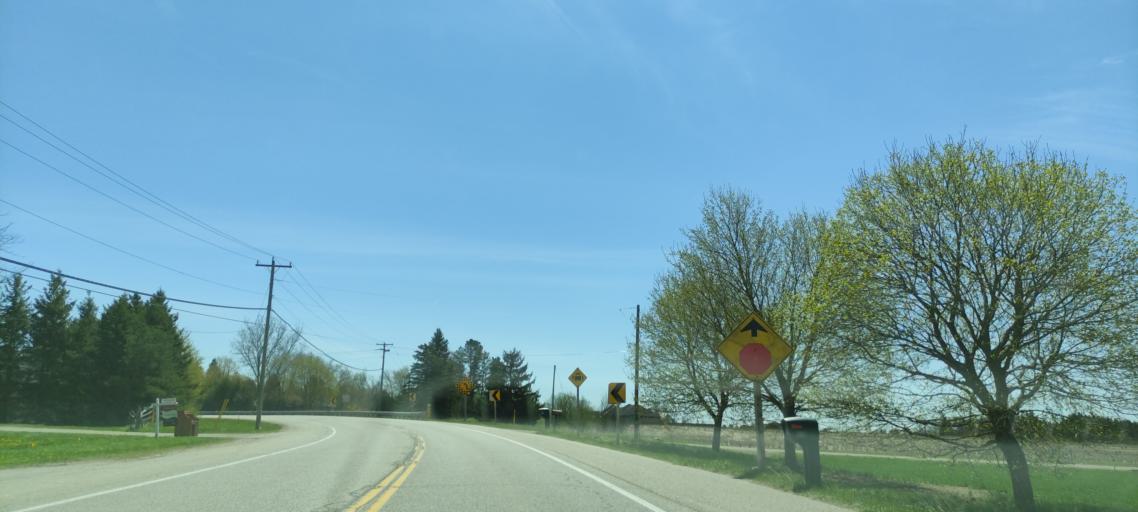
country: CA
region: Ontario
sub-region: Wellington County
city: Guelph
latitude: 43.5936
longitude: -80.3116
